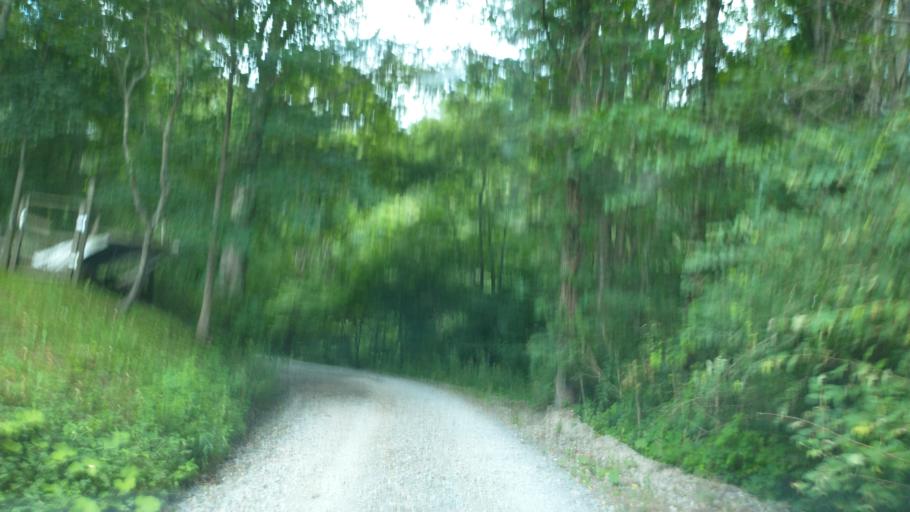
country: US
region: West Virginia
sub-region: Mercer County
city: Athens
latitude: 37.4362
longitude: -81.0035
